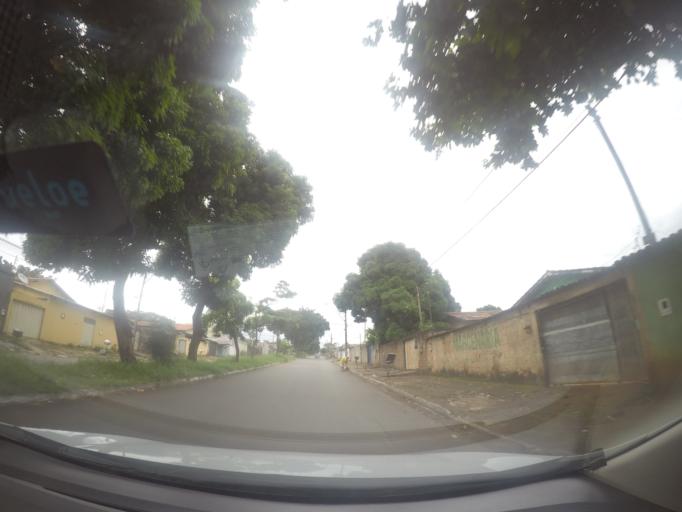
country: BR
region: Goias
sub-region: Goiania
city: Goiania
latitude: -16.6164
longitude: -49.3001
